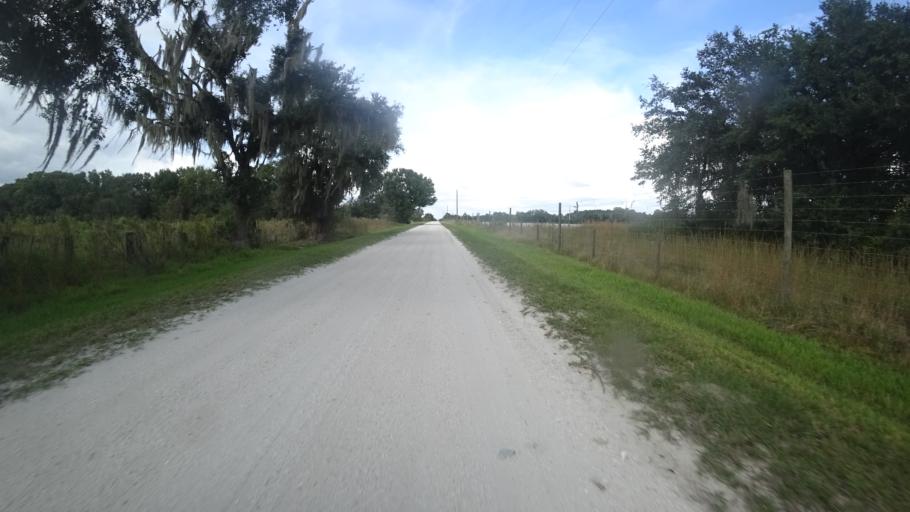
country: US
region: Florida
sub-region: Hillsborough County
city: Wimauma
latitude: 27.5499
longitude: -82.1745
